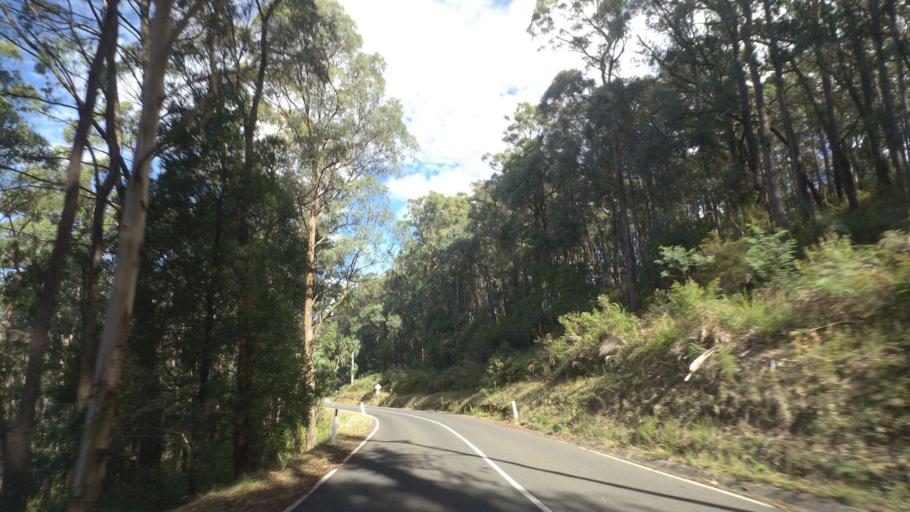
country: AU
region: Victoria
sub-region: Cardinia
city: Gembrook
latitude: -37.9761
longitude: 145.5827
